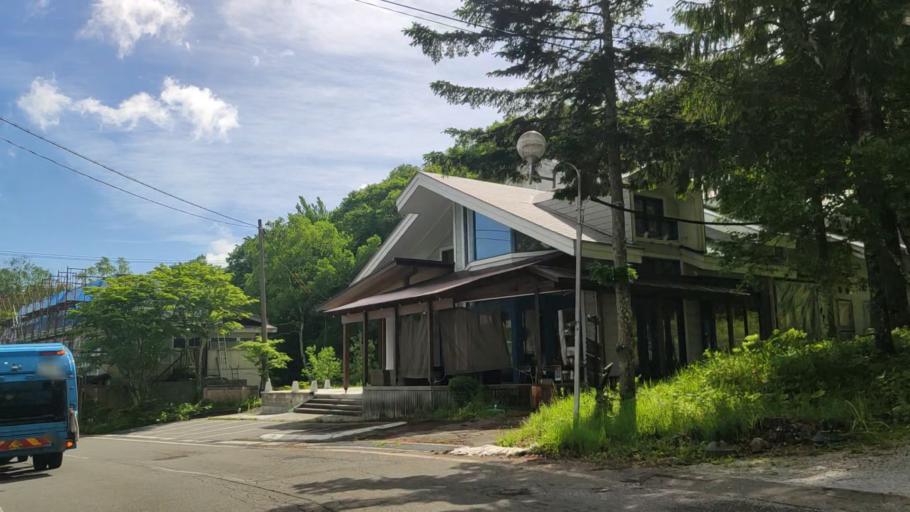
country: JP
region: Nagano
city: Chino
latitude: 36.1035
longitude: 138.2389
